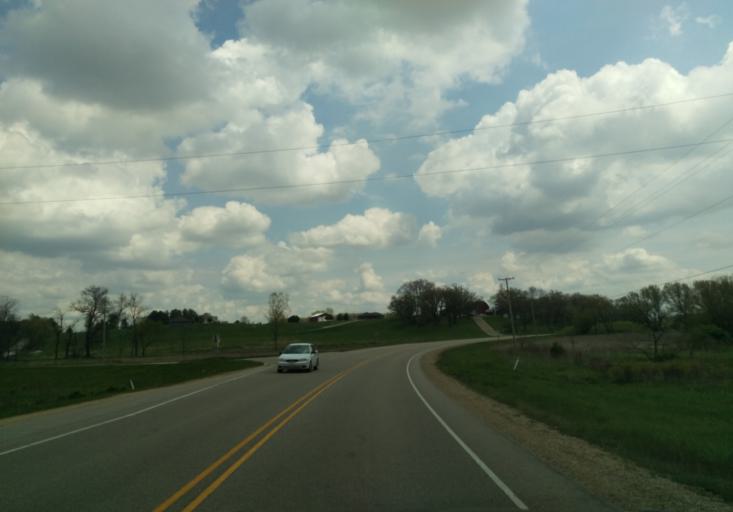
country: US
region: Wisconsin
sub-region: Dane County
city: Mount Horeb
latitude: 42.9625
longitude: -89.6740
